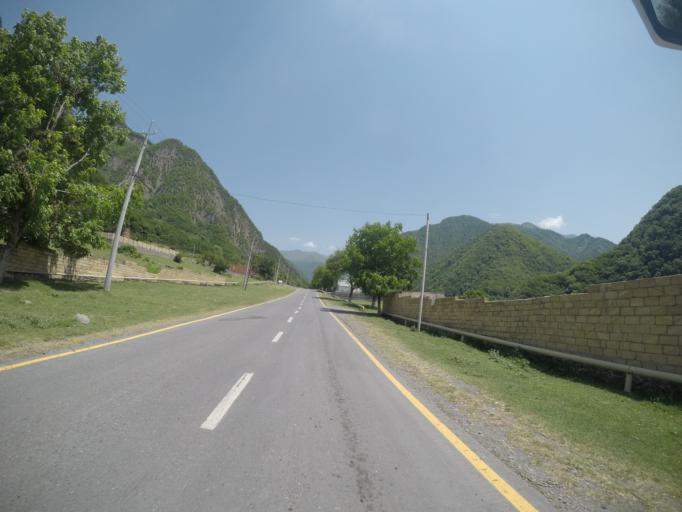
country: AZ
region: Qakh Rayon
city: Qaxbas
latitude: 41.4530
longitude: 47.0113
